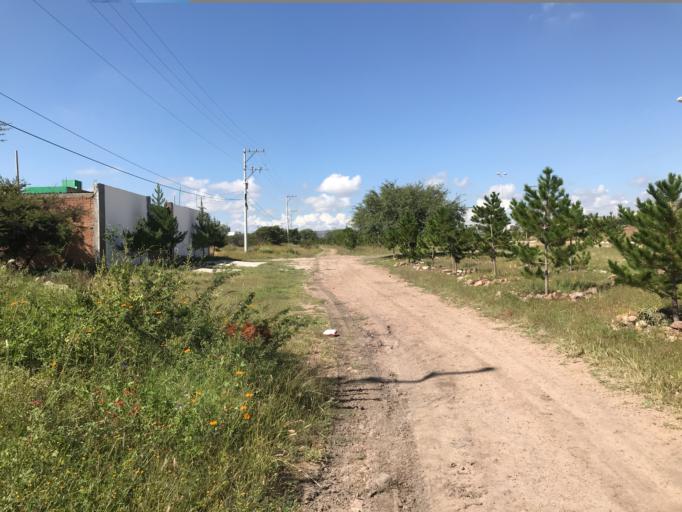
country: MX
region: Durango
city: Victoria de Durango
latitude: 24.0194
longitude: -104.7052
